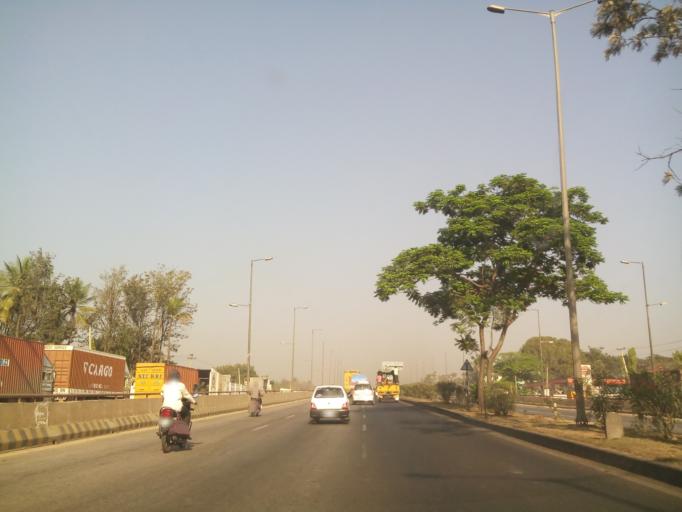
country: IN
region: Karnataka
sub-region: Bangalore Rural
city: Nelamangala
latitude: 13.0579
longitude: 77.4693
